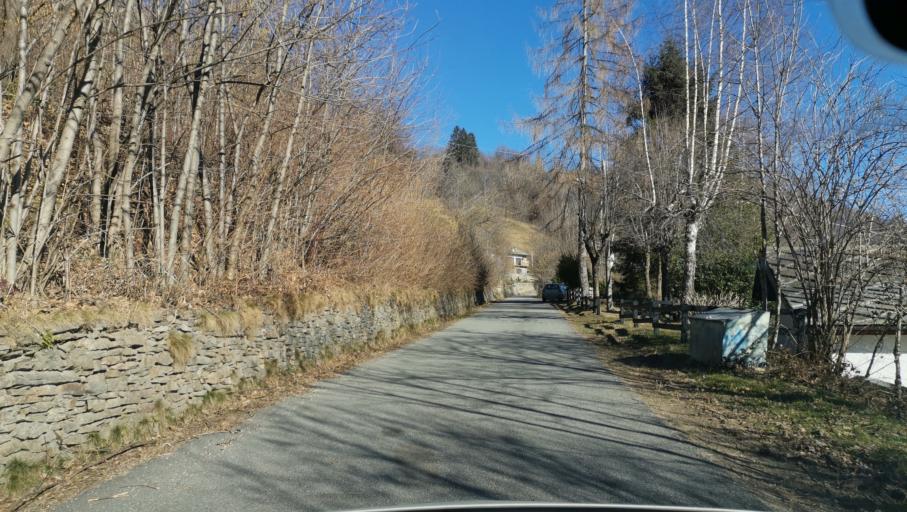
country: IT
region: Piedmont
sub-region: Provincia di Torino
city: Rora
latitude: 44.7921
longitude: 7.1946
